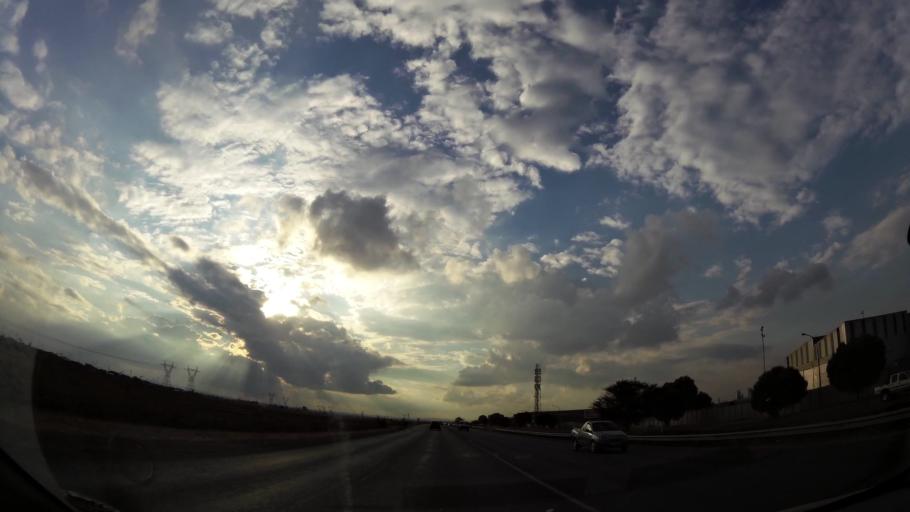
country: ZA
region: Gauteng
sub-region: Sedibeng District Municipality
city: Vanderbijlpark
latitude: -26.6829
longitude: 27.7977
